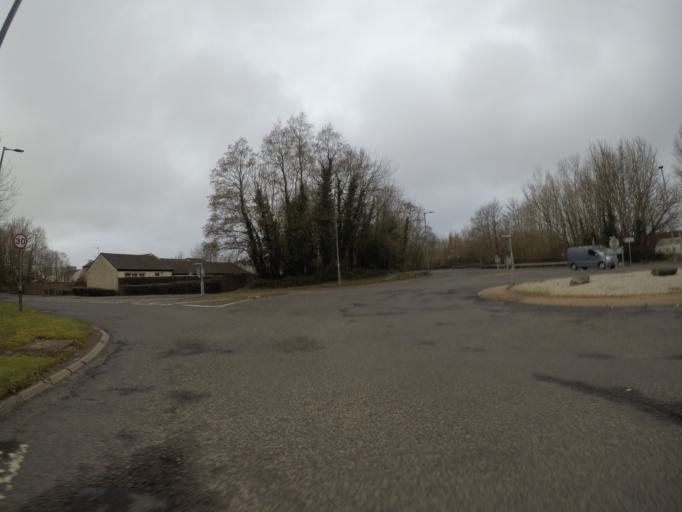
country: GB
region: Scotland
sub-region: North Ayrshire
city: Irvine
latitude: 55.6312
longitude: -4.6353
